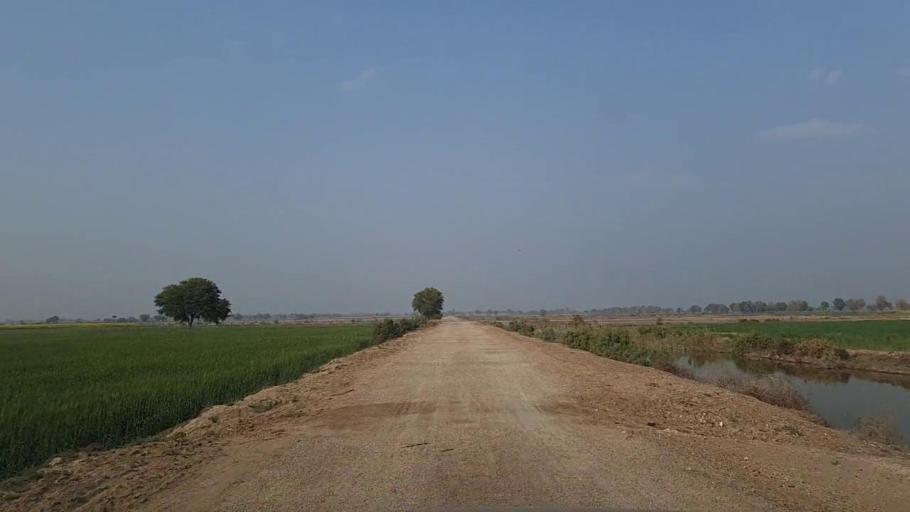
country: PK
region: Sindh
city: Nawabshah
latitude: 26.3385
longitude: 68.4738
